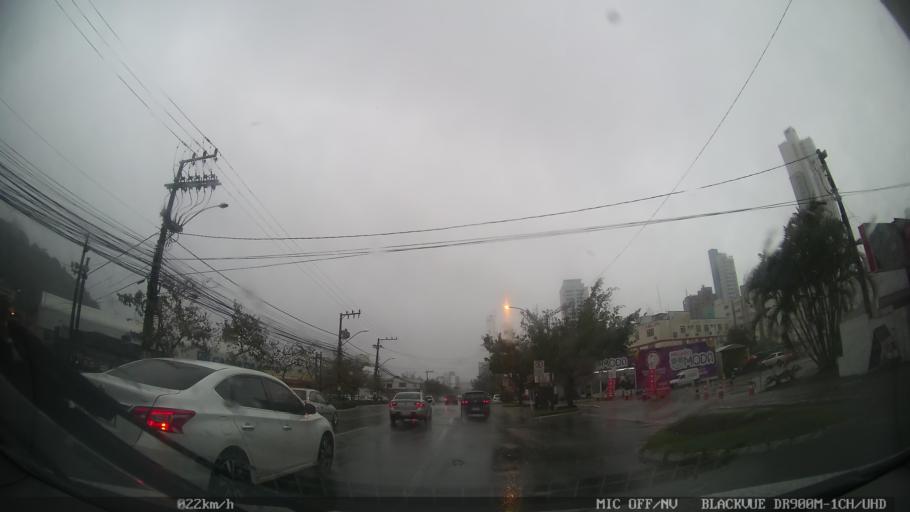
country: BR
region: Santa Catarina
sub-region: Balneario Camboriu
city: Balneario Camboriu
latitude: -26.9865
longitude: -48.6397
